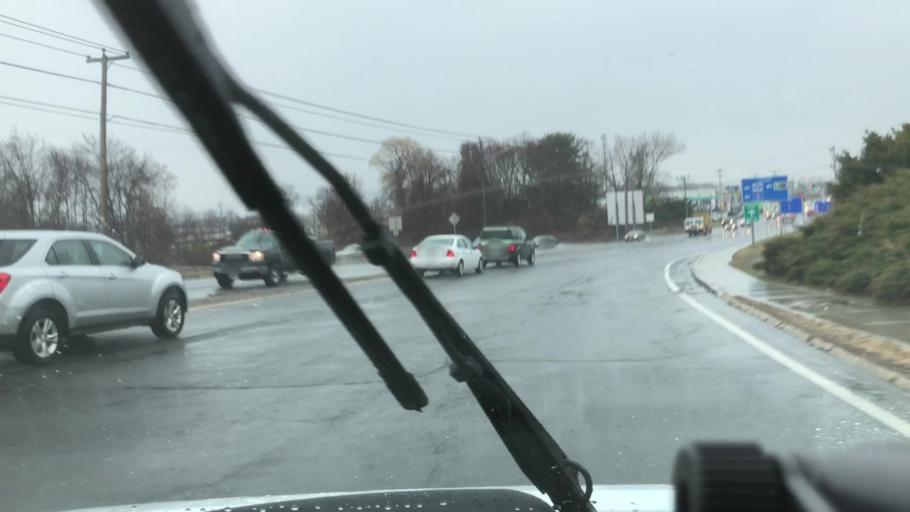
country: US
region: Massachusetts
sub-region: Hampshire County
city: Northampton
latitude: 42.3394
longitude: -72.6383
